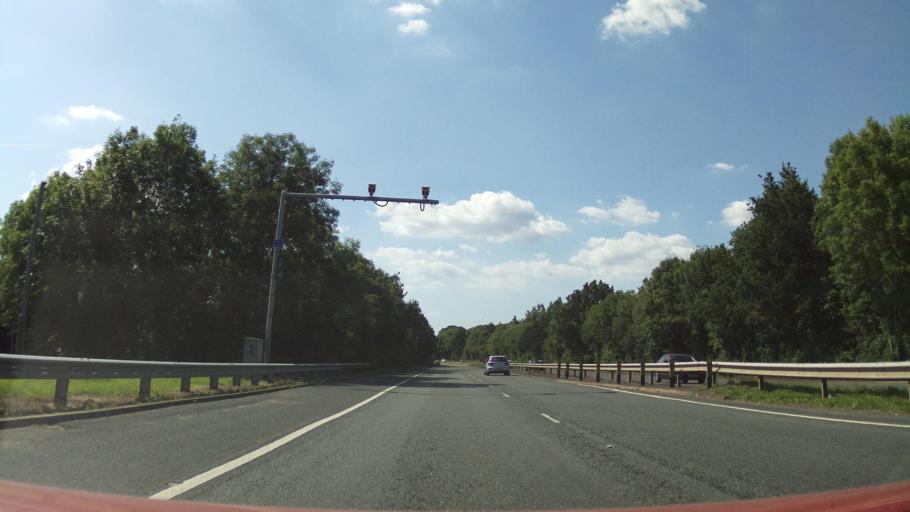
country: GB
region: England
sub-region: Worcestershire
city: Bromsgrove
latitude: 52.3332
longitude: -2.0386
